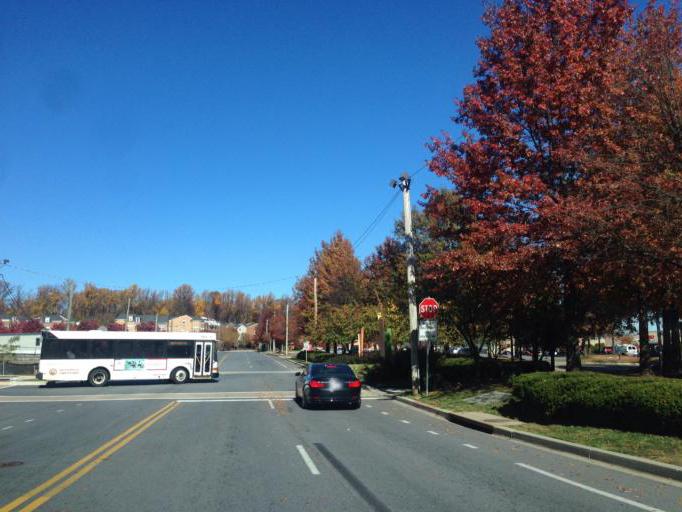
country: US
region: Maryland
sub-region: Howard County
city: Columbia
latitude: 39.2141
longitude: -76.8648
